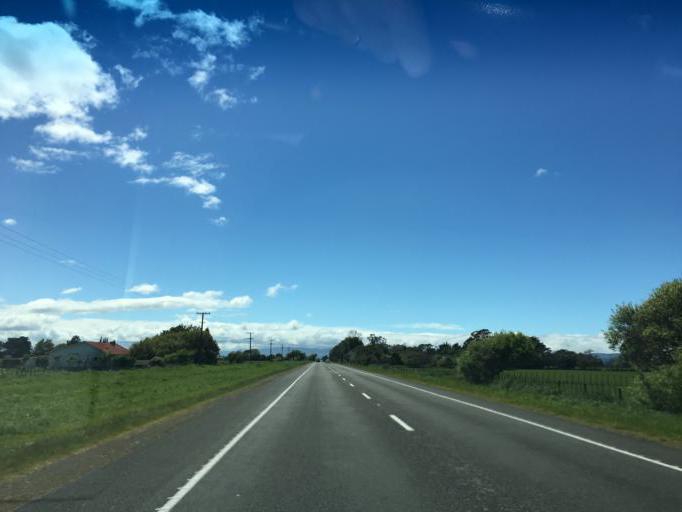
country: NZ
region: Manawatu-Wanganui
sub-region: Palmerston North City
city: Palmerston North
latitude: -40.3947
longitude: 175.5182
